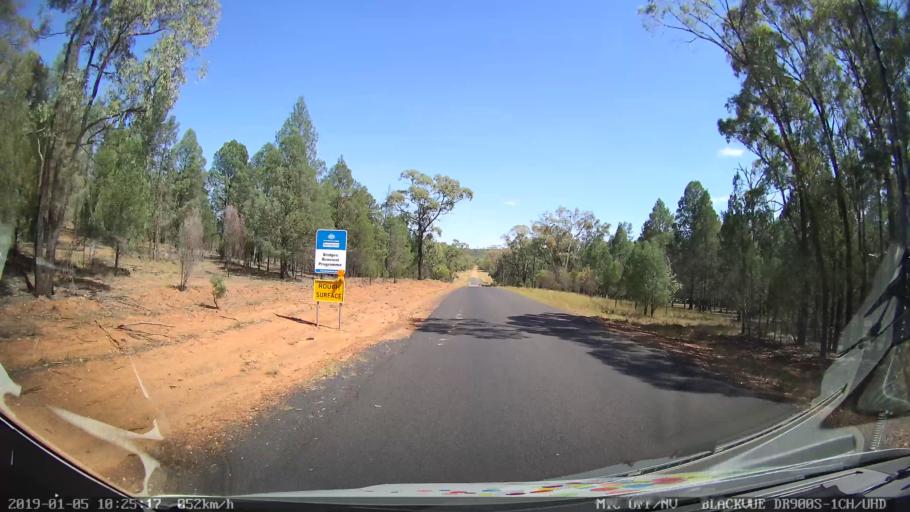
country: AU
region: New South Wales
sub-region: Gilgandra
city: Gilgandra
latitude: -31.5625
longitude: 148.9601
